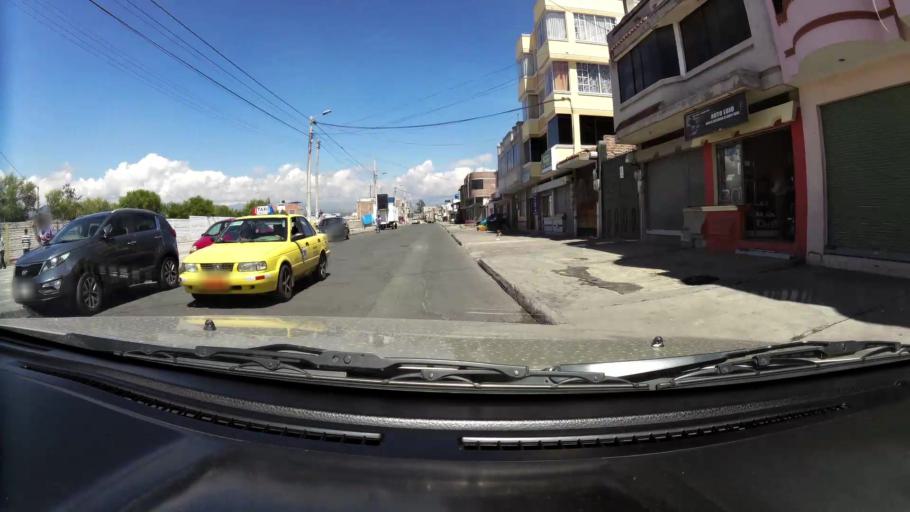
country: EC
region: Chimborazo
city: Riobamba
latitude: -1.6652
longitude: -78.6446
